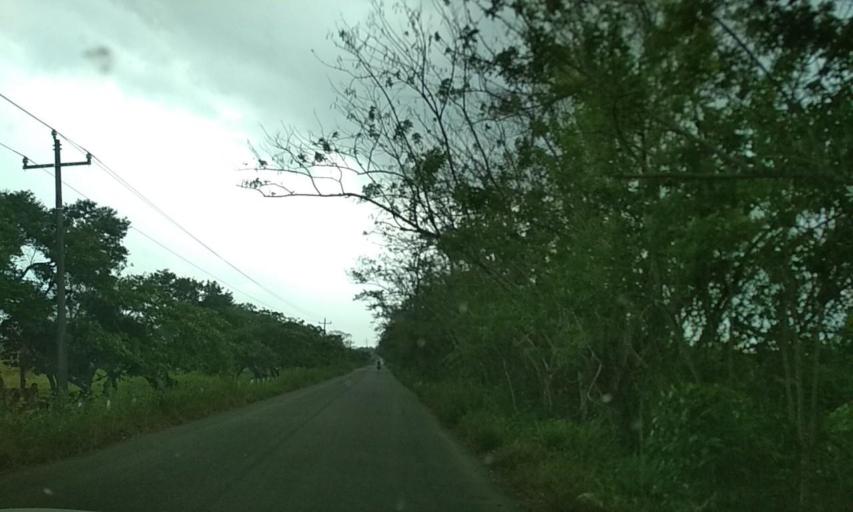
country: MX
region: Tabasco
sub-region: Huimanguillo
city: Francisco Rueda
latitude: 17.5576
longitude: -94.1198
